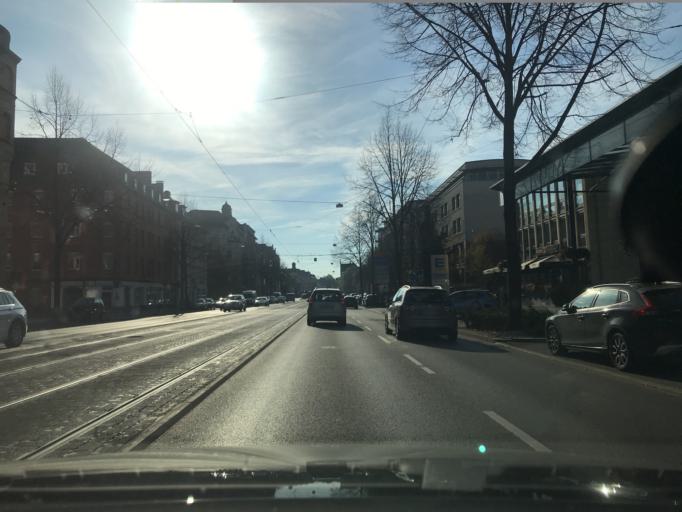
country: DE
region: Hesse
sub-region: Regierungsbezirk Kassel
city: Kassel
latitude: 51.3016
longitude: 9.4825
